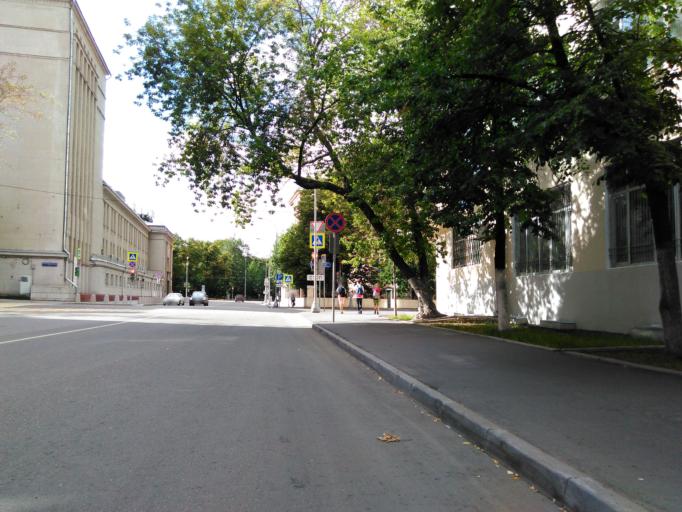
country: RU
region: Moskovskaya
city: Dorogomilovo
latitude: 55.7317
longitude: 37.5778
